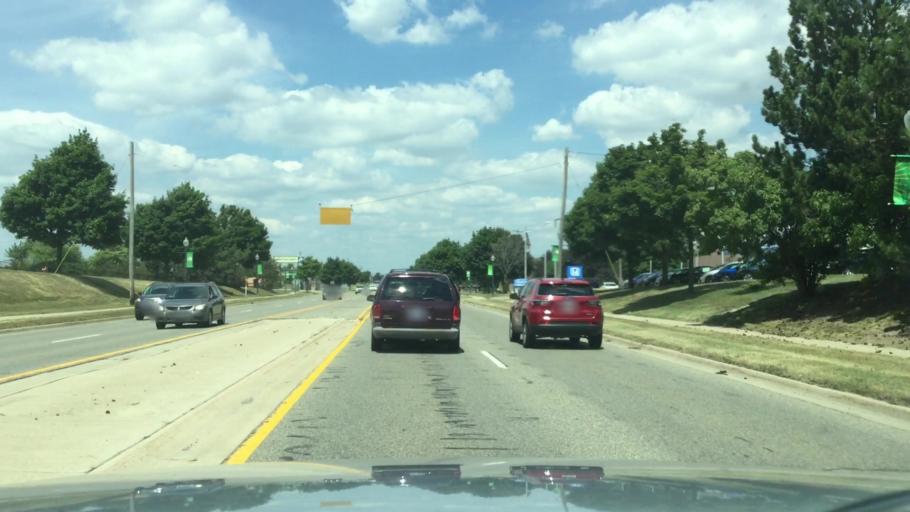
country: US
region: Michigan
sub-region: Genesee County
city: Grand Blanc
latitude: 42.9342
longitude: -83.6381
